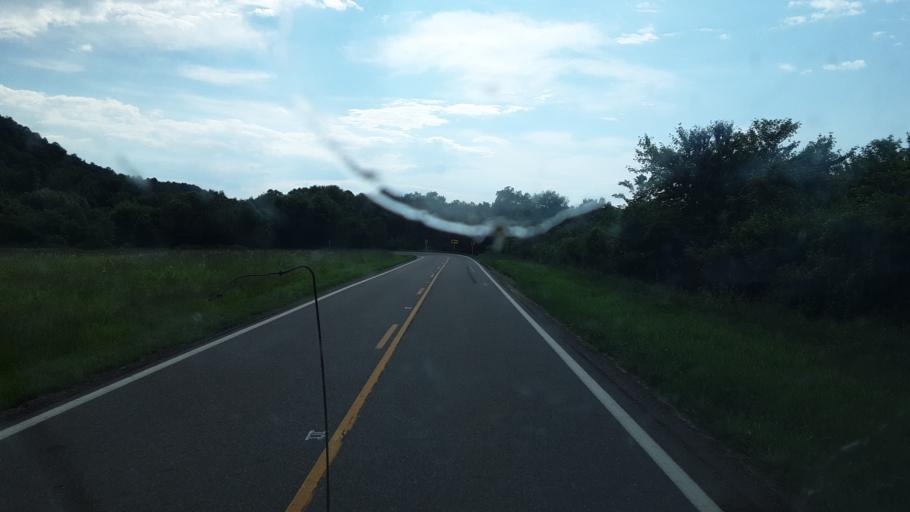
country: US
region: Ohio
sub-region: Coshocton County
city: Coshocton
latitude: 40.3772
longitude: -81.9653
